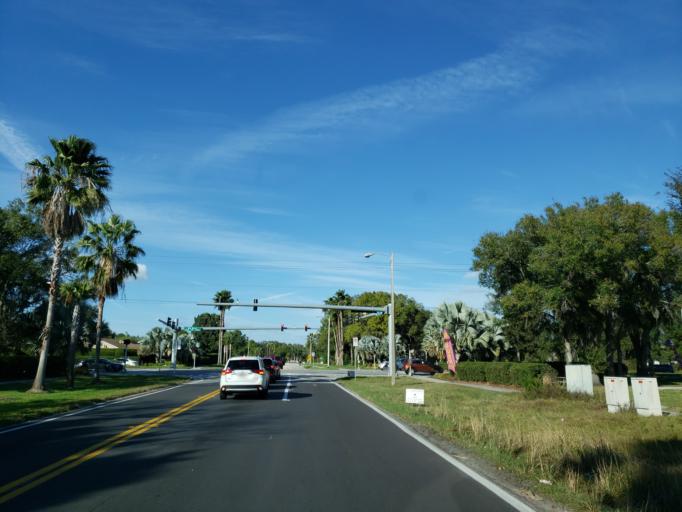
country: US
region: Florida
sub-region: Hillsborough County
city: Balm
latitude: 27.7915
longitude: -82.3178
